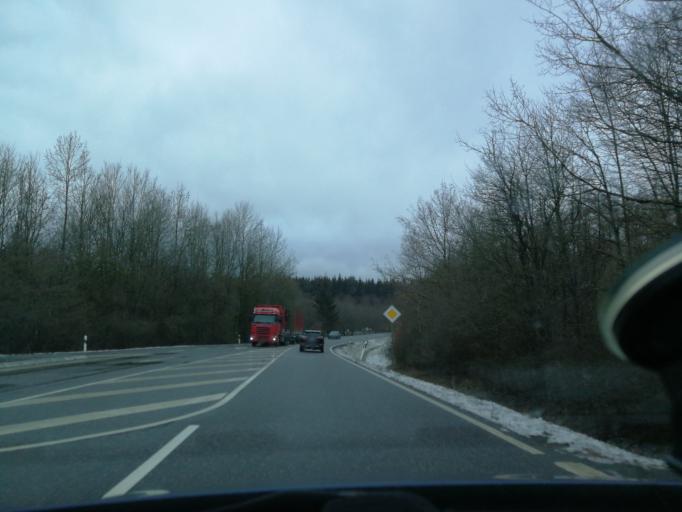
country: DE
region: North Rhine-Westphalia
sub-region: Regierungsbezirk Koln
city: Blankenheim
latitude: 50.4505
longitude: 6.7066
